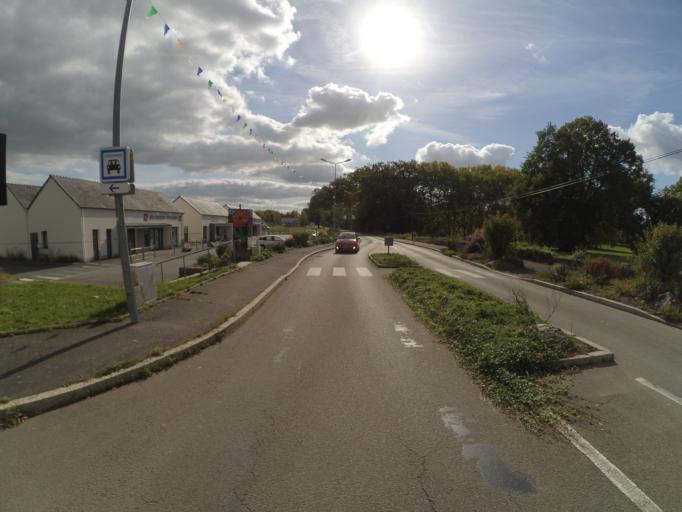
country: FR
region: Pays de la Loire
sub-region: Departement de la Loire-Atlantique
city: Casson
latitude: 47.3846
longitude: -1.5599
